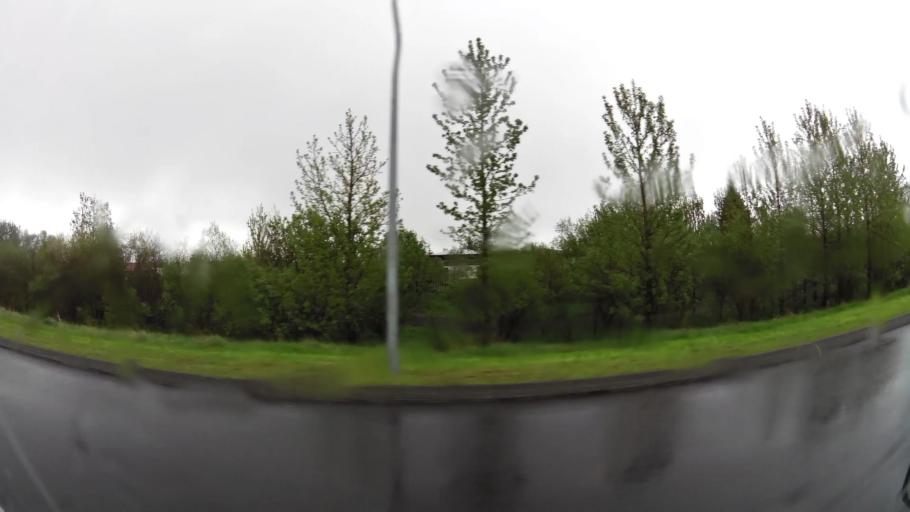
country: IS
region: South
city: Selfoss
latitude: 63.9268
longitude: -21.0073
